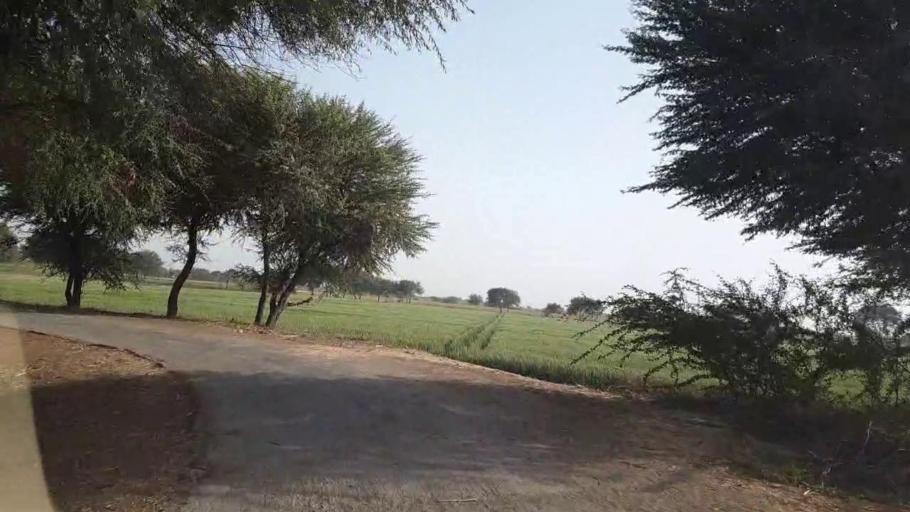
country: PK
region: Sindh
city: Tando Ghulam Ali
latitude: 25.0807
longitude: 68.8957
